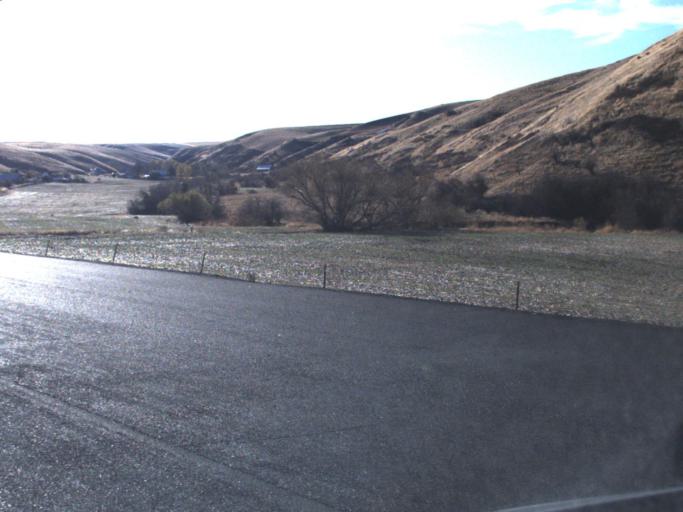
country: US
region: Washington
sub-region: Garfield County
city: Pomeroy
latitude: 46.4656
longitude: -117.4773
